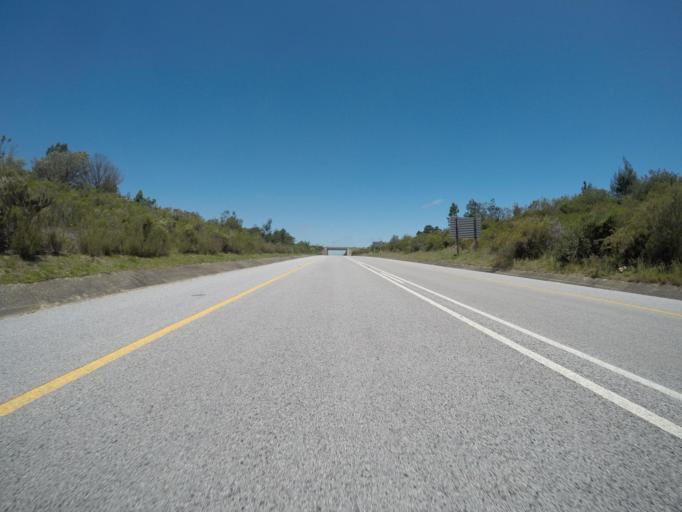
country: ZA
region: Eastern Cape
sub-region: Cacadu District Municipality
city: Kruisfontein
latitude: -34.0274
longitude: 24.5988
